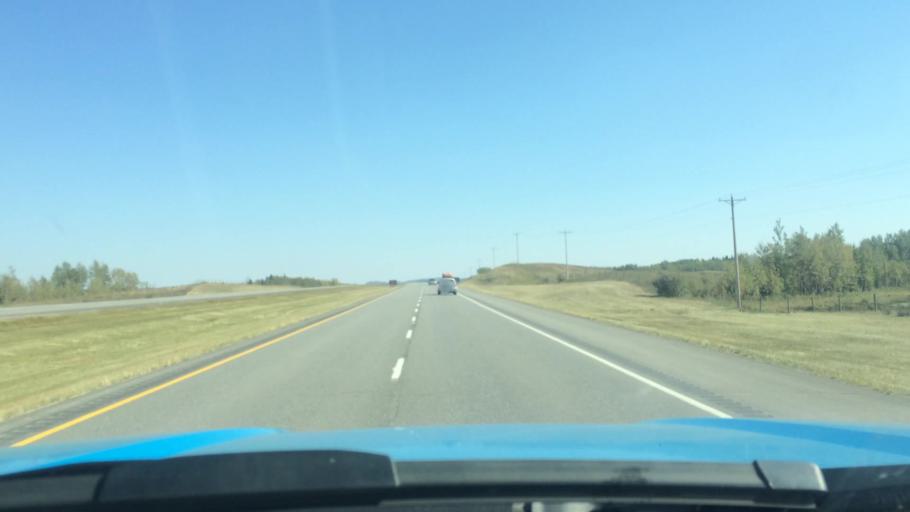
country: CA
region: Alberta
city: Cochrane
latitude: 51.1236
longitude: -114.6757
